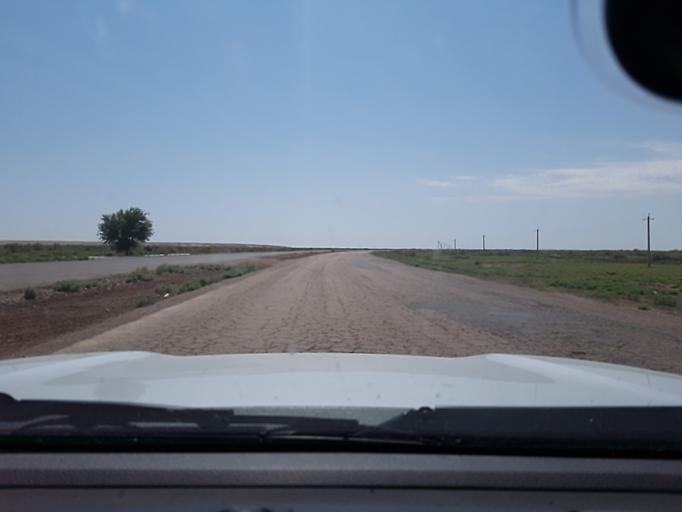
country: TM
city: Akdepe
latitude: 41.6342
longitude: 58.6630
